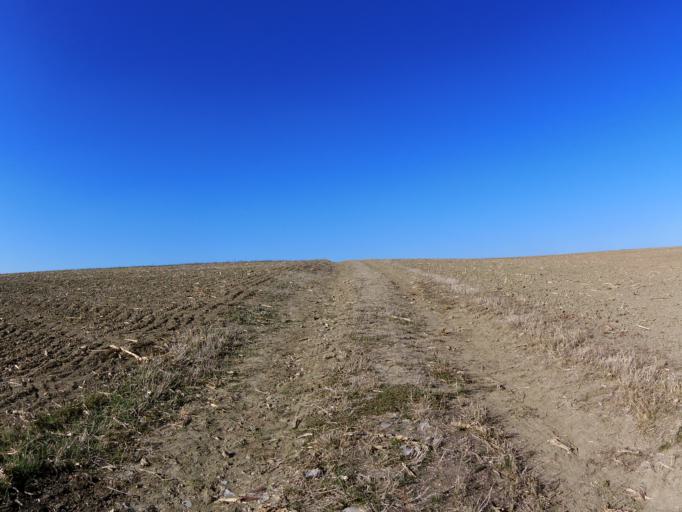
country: DE
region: Bavaria
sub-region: Regierungsbezirk Unterfranken
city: Eibelstadt
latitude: 49.7065
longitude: 9.9771
